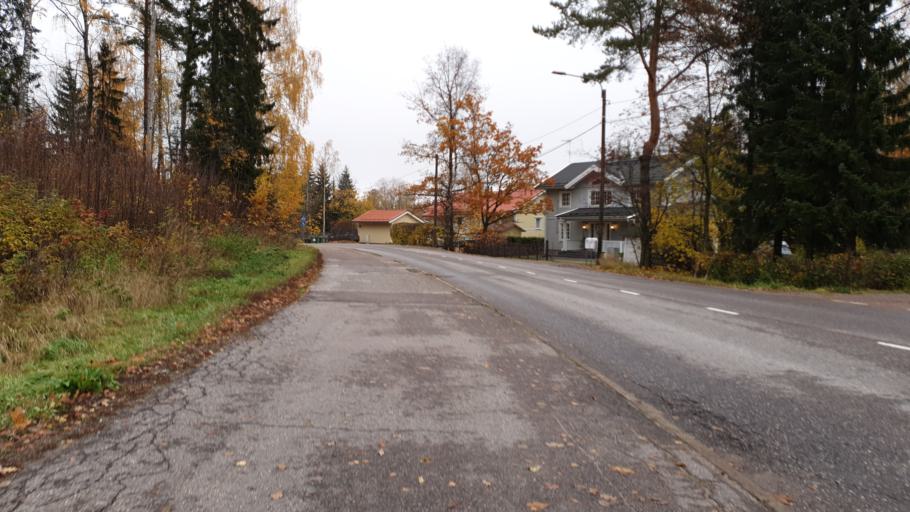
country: FI
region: Uusimaa
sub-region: Helsinki
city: Kilo
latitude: 60.2615
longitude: 24.8170
